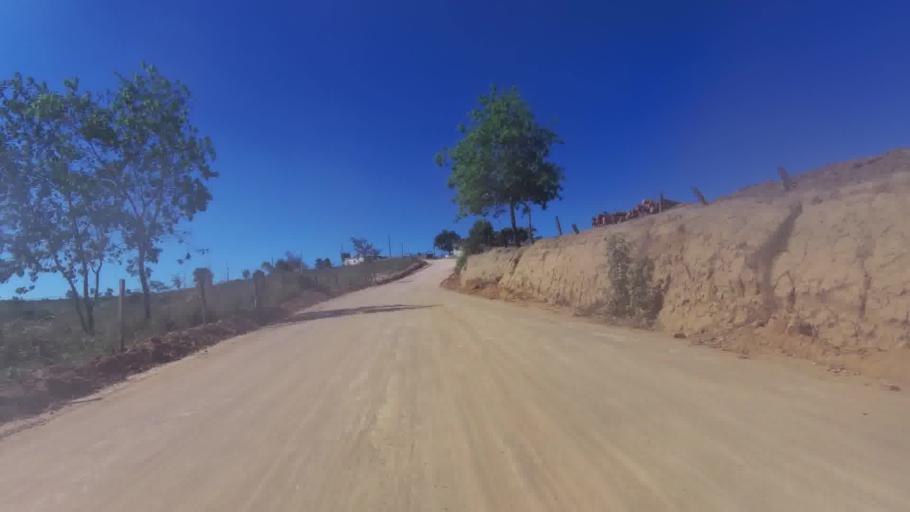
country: BR
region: Espirito Santo
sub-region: Marataizes
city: Marataizes
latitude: -21.1462
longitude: -40.9839
